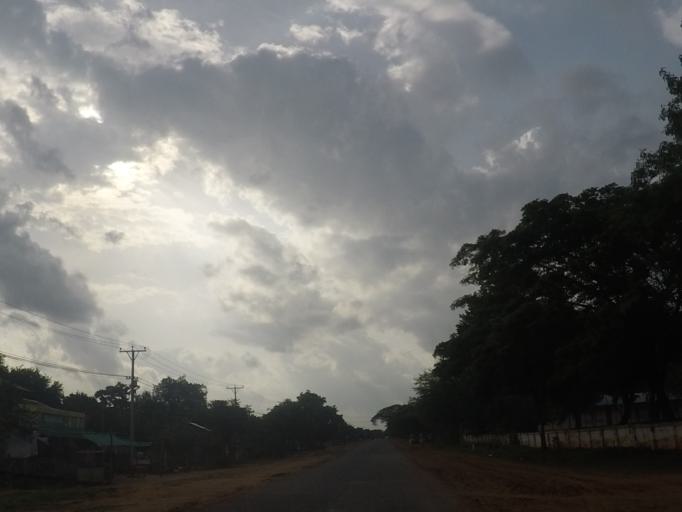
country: MM
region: Mandalay
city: Yamethin
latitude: 20.5077
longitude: 95.7722
